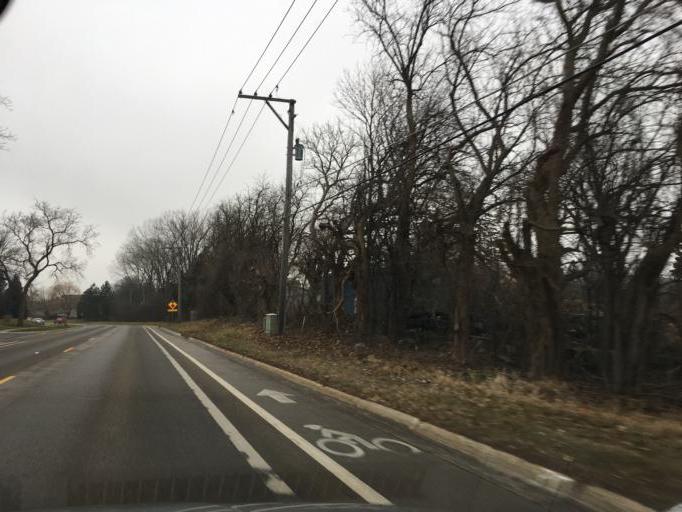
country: US
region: Illinois
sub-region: McHenry County
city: Lakewood
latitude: 42.2190
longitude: -88.3475
